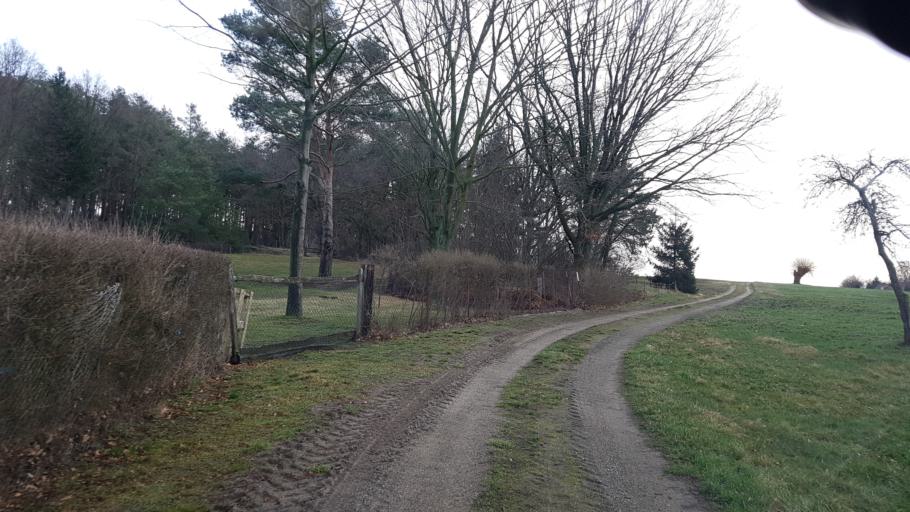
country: DE
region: Brandenburg
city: Falkenberg
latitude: 51.6422
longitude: 13.2988
